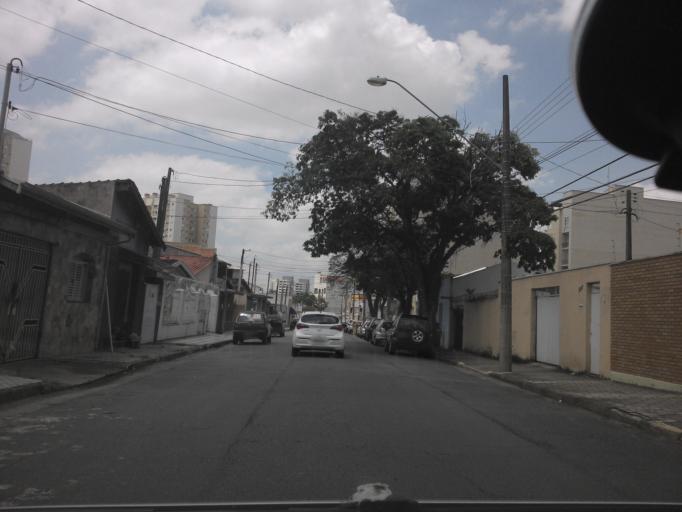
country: BR
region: Sao Paulo
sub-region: Taubate
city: Taubate
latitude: -23.0349
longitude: -45.5634
